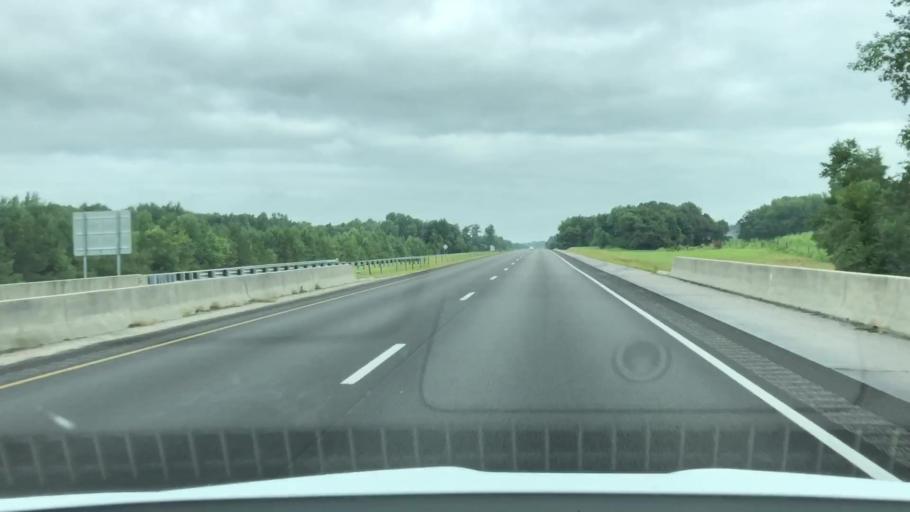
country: US
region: North Carolina
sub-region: Wayne County
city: Fremont
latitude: 35.5618
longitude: -77.9876
